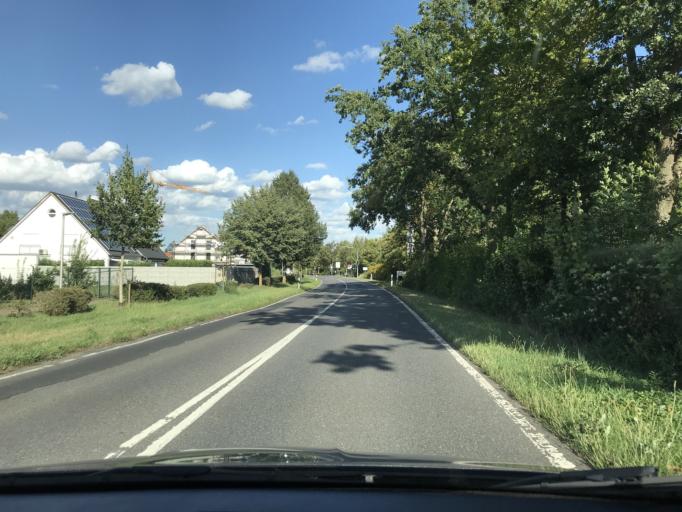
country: DE
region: Bavaria
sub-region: Regierungsbezirk Unterfranken
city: Grossostheim
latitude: 49.9212
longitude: 9.0660
